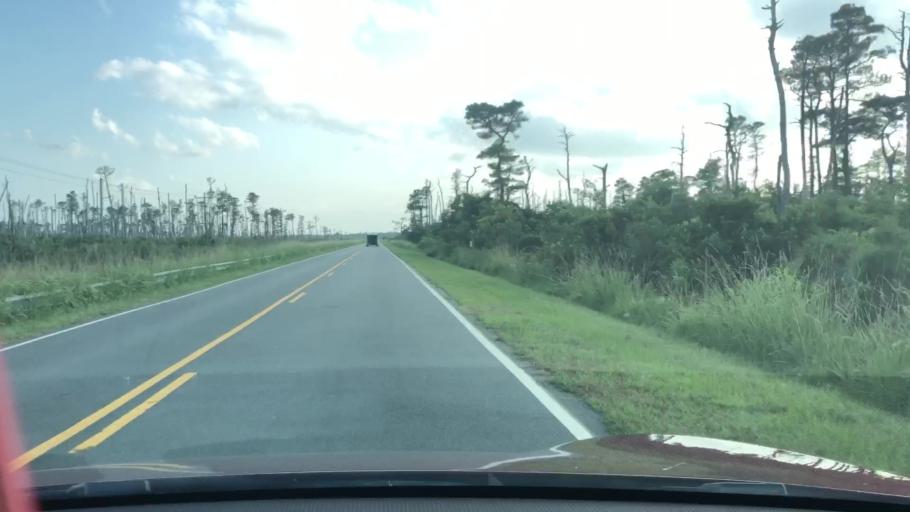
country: US
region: North Carolina
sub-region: Dare County
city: Wanchese
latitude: 35.6302
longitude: -75.7817
